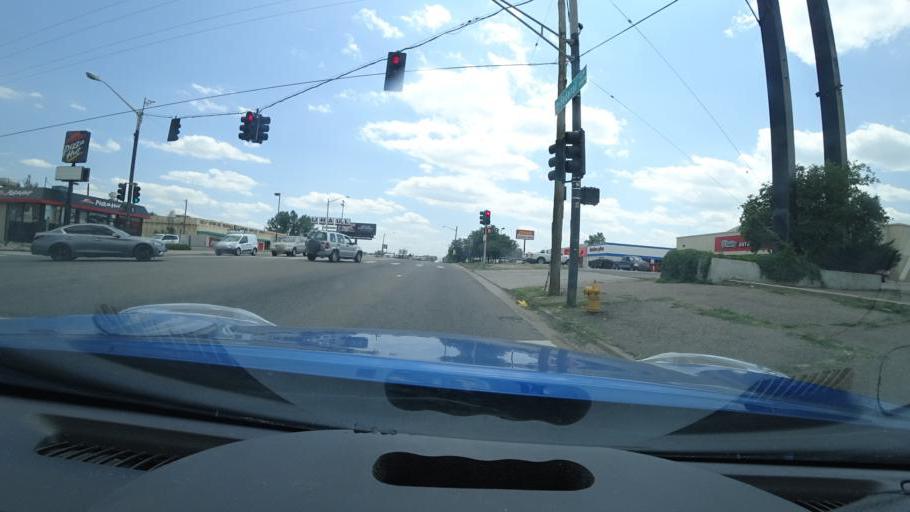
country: US
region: Colorado
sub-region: Arapahoe County
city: Sheridan
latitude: 39.6751
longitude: -105.0251
